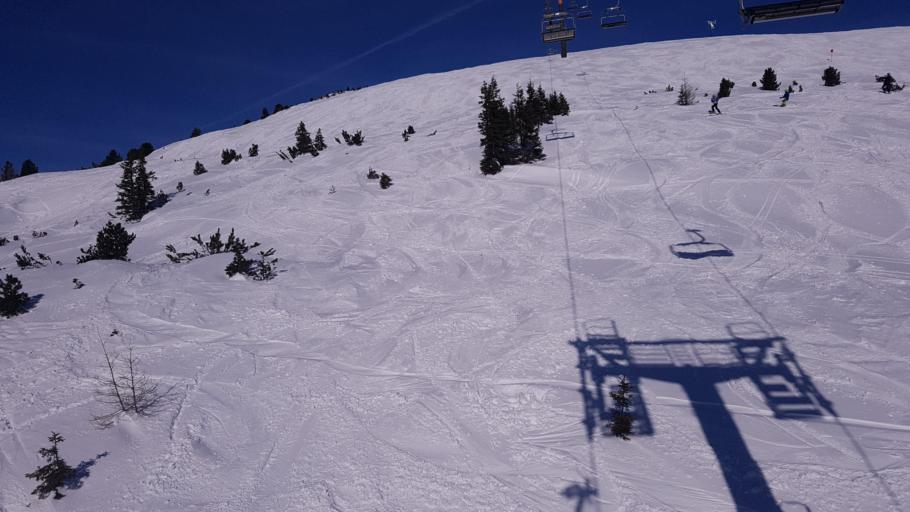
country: AT
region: Salzburg
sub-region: Politischer Bezirk Zell am See
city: Neukirchen am Grossvenediger
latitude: 47.2787
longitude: 12.2656
